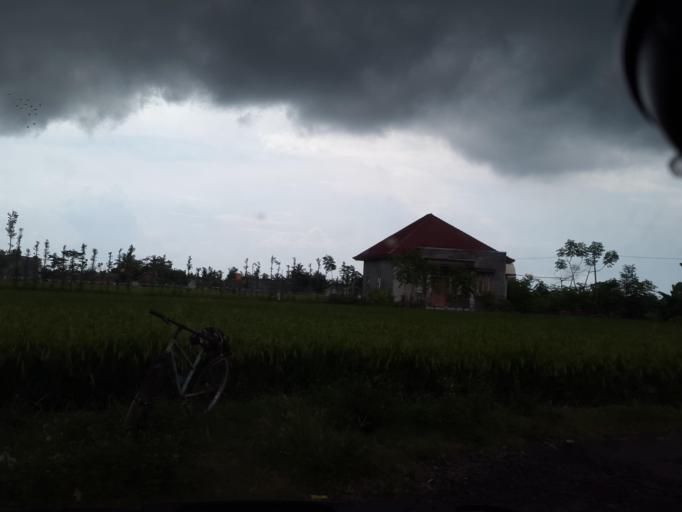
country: ID
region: West Nusa Tenggara
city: Karangparwa
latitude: -8.6208
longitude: 116.1050
